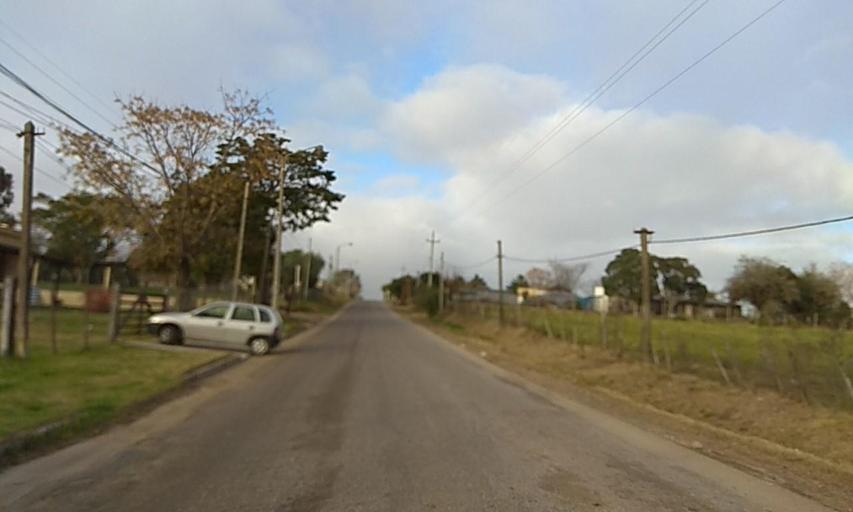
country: UY
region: Florida
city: Florida
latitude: -34.0809
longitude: -56.2118
